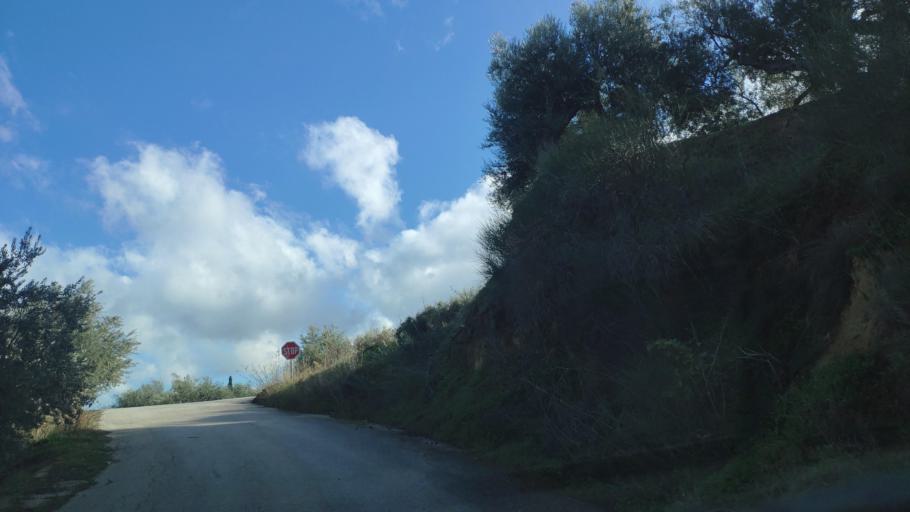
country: GR
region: West Greece
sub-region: Nomos Achaias
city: Aiyira
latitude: 38.1043
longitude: 22.4456
